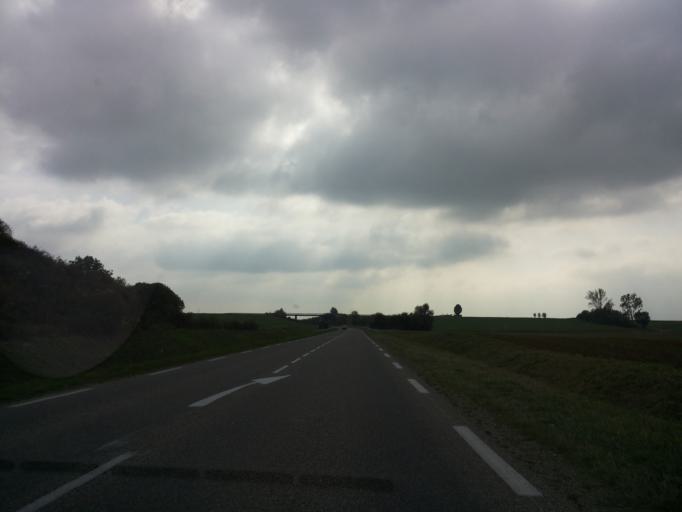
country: FR
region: Lorraine
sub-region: Departement de la Moselle
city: Solgne
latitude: 48.9134
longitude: 6.3374
